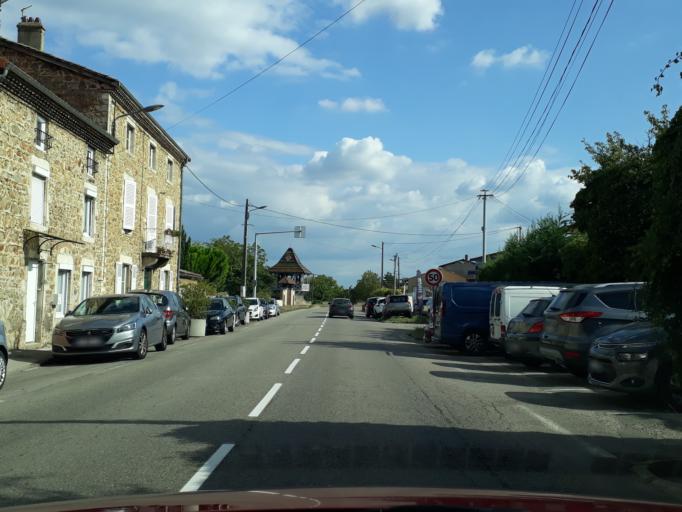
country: FR
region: Rhone-Alpes
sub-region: Departement de la Loire
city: Saint-Pierre-de-Boeuf
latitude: 45.3820
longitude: 4.7500
